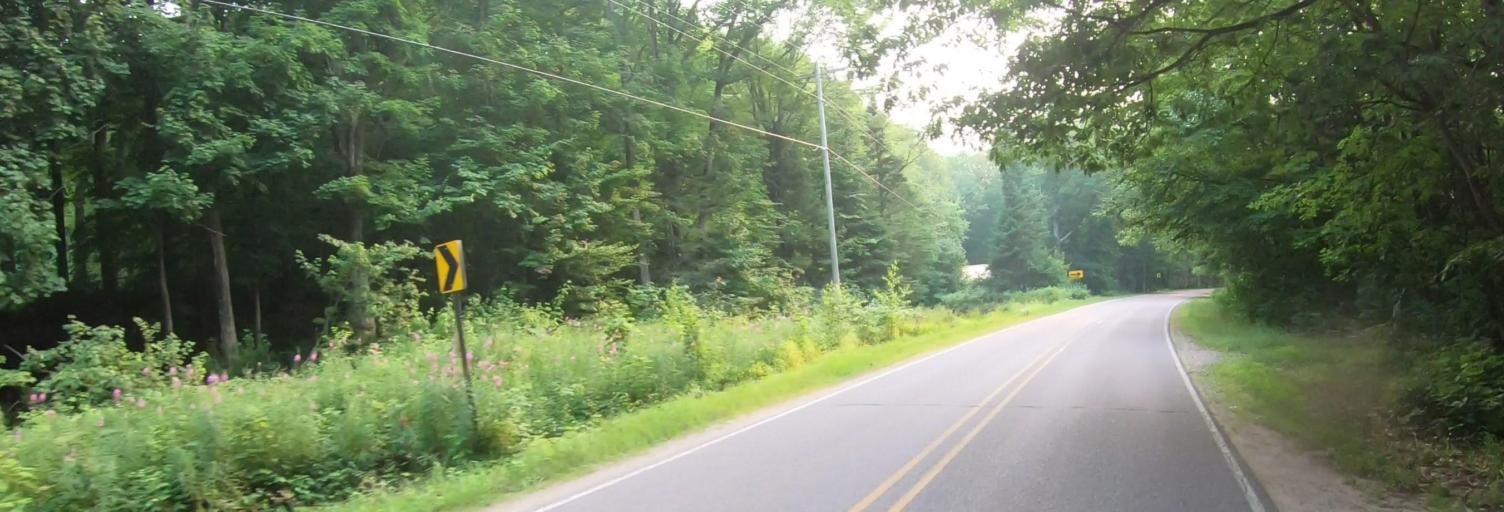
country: US
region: Michigan
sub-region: Chippewa County
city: Sault Ste. Marie
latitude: 46.4813
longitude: -84.6555
